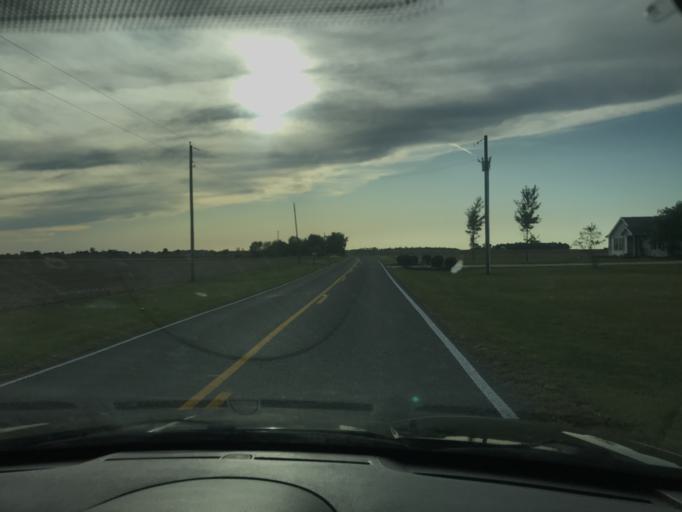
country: US
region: Ohio
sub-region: Logan County
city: West Liberty
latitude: 40.2134
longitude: -83.6890
